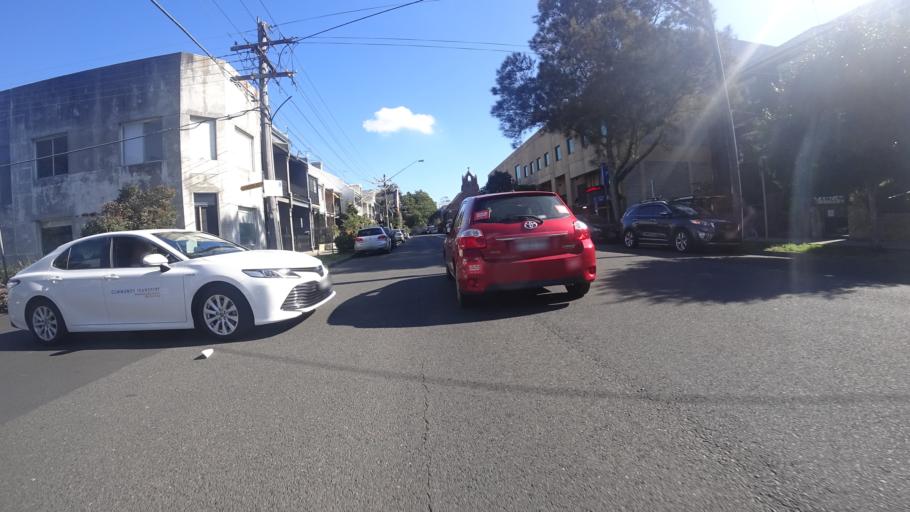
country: AU
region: New South Wales
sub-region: Waverley
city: Bondi Junction
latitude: -33.8932
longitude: 151.2455
